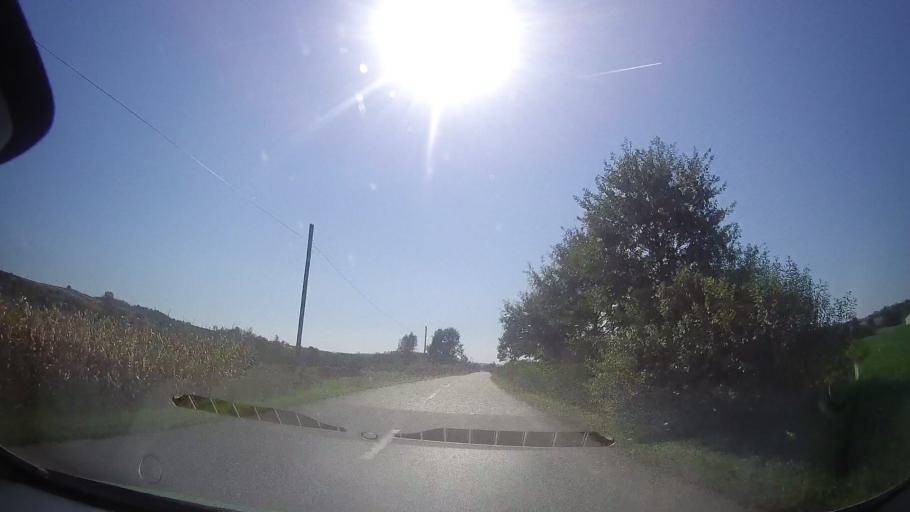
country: RO
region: Timis
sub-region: Comuna Ohaba Lunga
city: Ohaba Lunga
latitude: 45.8800
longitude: 21.9643
